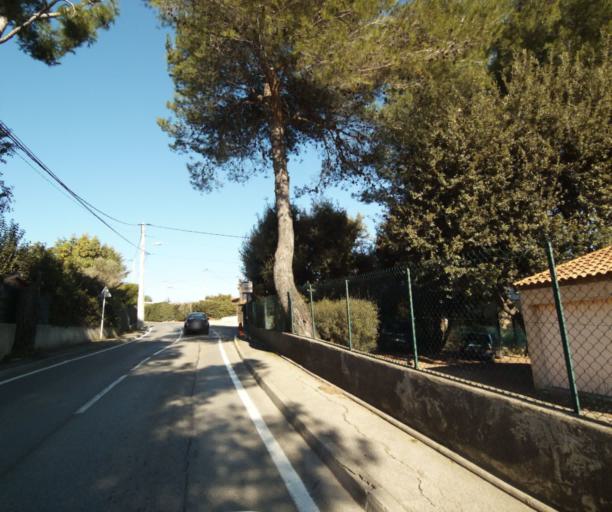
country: FR
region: Provence-Alpes-Cote d'Azur
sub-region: Departement des Alpes-Maritimes
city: Biot
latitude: 43.6064
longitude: 7.0893
